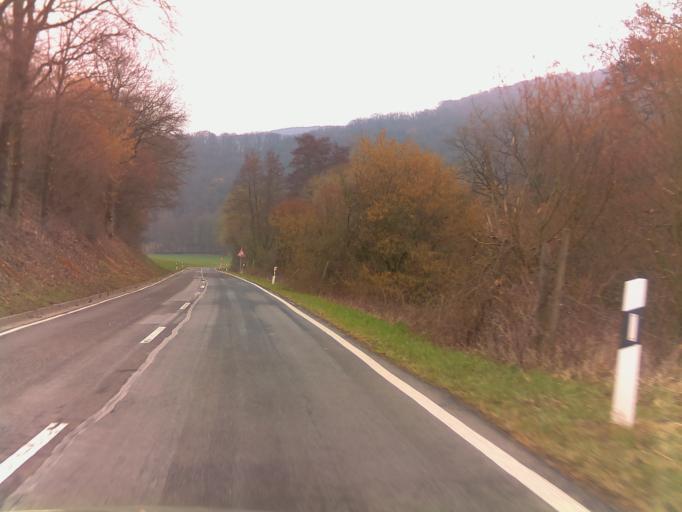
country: DE
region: Rheinland-Pfalz
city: Sankt Alban
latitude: 49.6916
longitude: 7.8567
